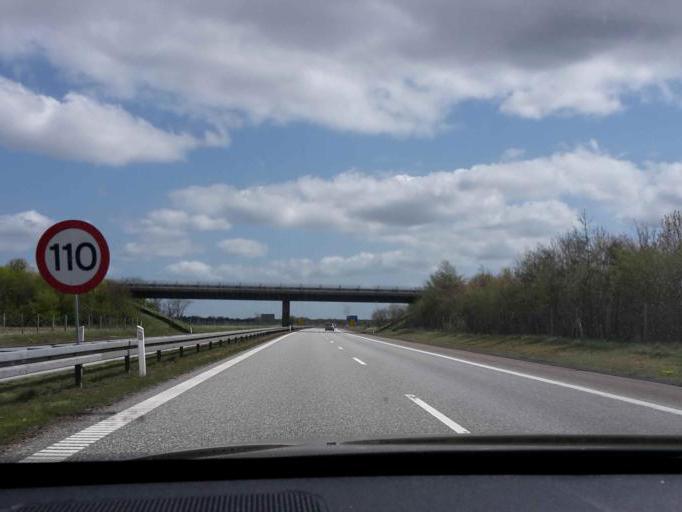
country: DK
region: South Denmark
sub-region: Esbjerg Kommune
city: Bramming
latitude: 55.5142
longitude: 8.7897
